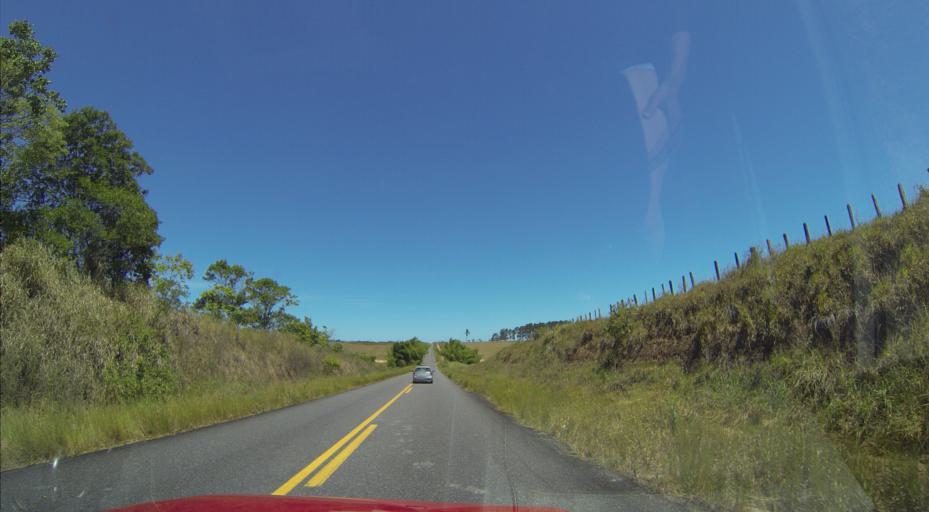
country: BR
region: Bahia
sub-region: Prado
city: Prado
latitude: -17.2292
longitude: -39.3750
